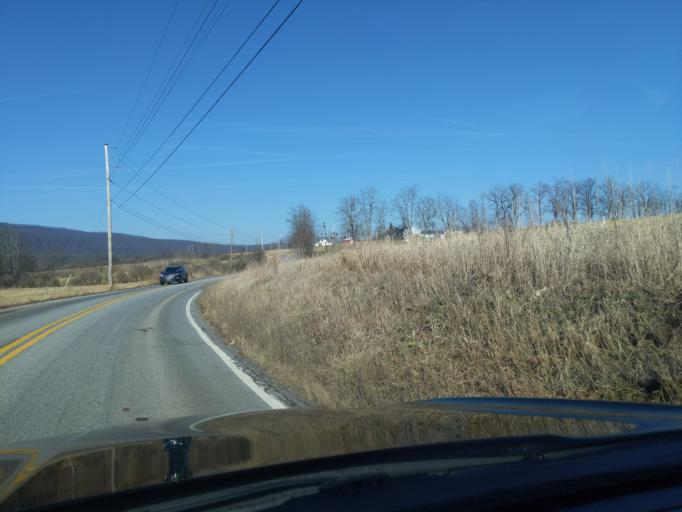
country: US
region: Pennsylvania
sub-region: Blair County
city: Tipton
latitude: 40.5844
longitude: -78.2639
